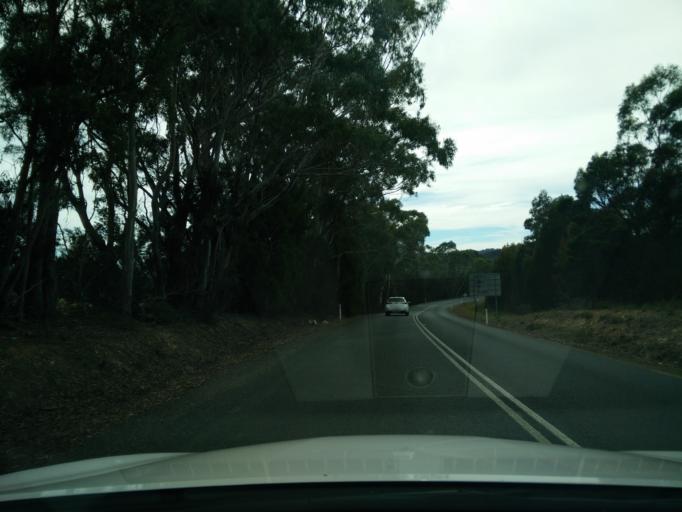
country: AU
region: Tasmania
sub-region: Break O'Day
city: St Helens
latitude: -41.9403
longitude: 148.2224
